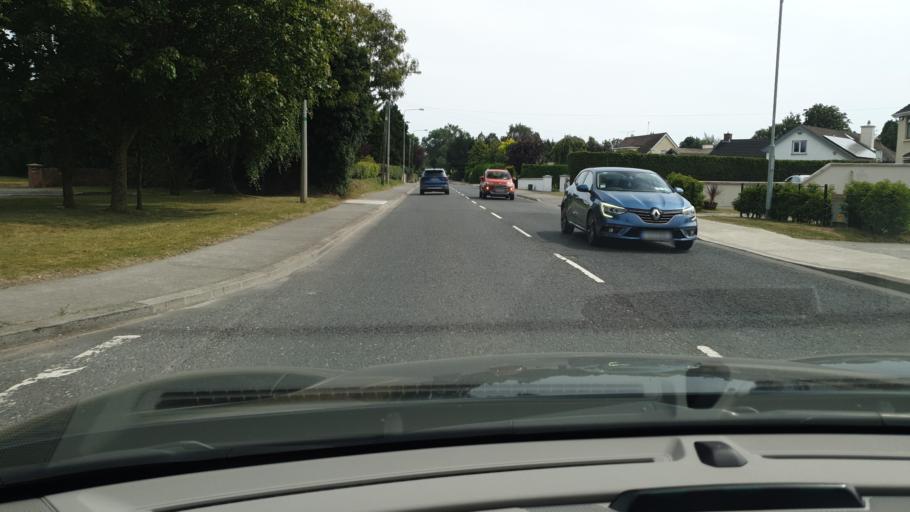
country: IE
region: Leinster
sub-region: An Mhi
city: Navan
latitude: 53.6501
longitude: -6.6617
